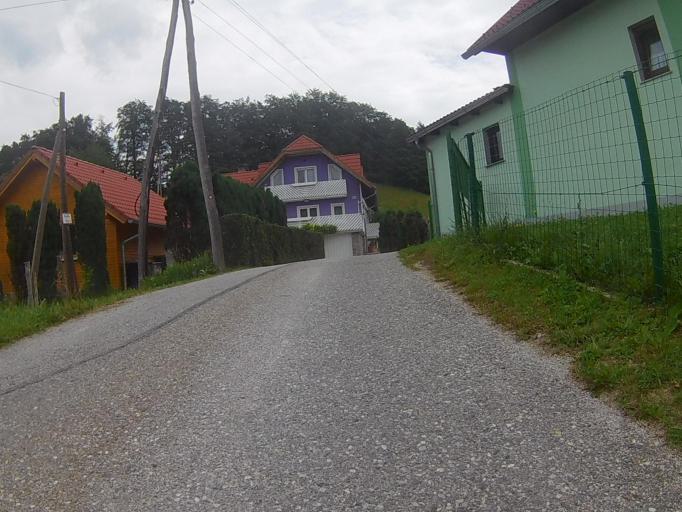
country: SI
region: Sentilj
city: Sentilj v Slov. Goricah
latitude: 46.6734
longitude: 15.6359
